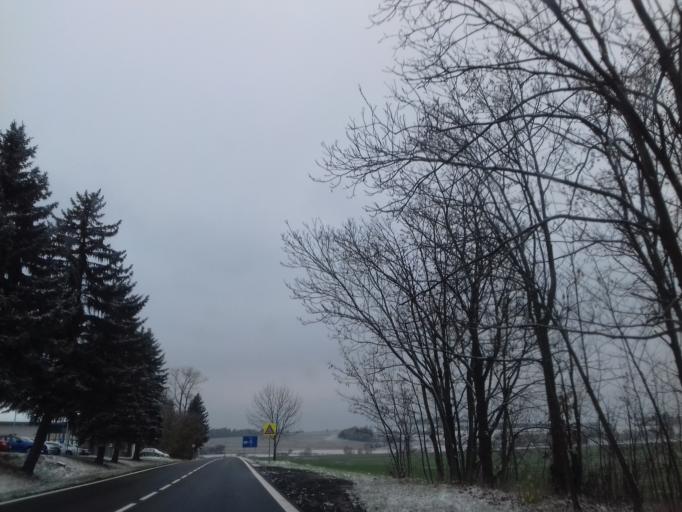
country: CZ
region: Plzensky
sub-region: Okres Domazlice
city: Domazlice
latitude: 49.4432
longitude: 12.9149
